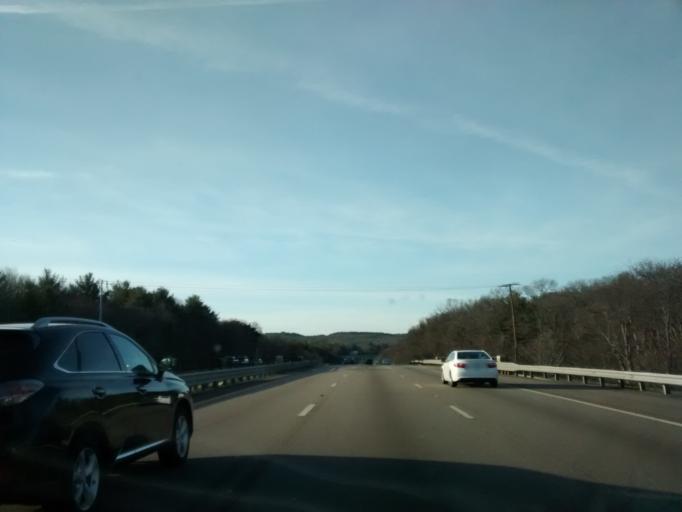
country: US
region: Massachusetts
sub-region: Norfolk County
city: Randolph
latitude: 42.1850
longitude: -71.0763
